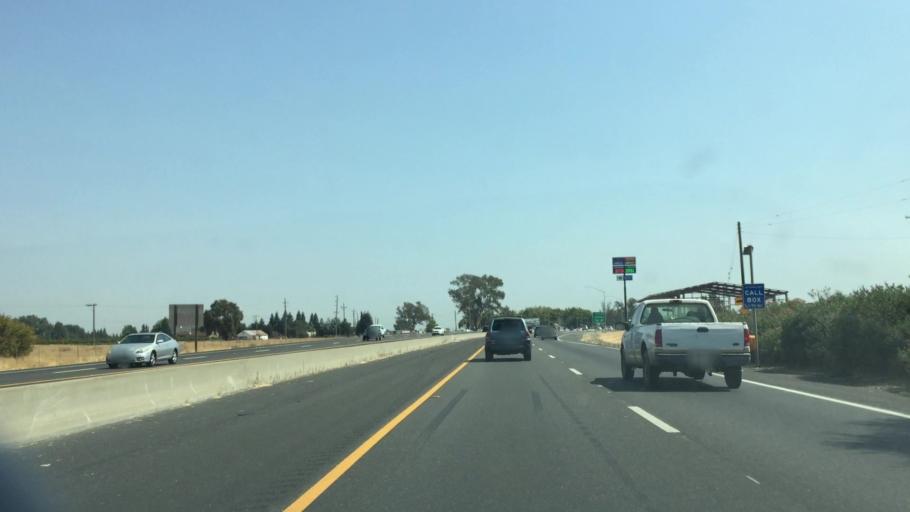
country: US
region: California
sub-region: San Joaquin County
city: Collierville
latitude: 38.2095
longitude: -121.2651
